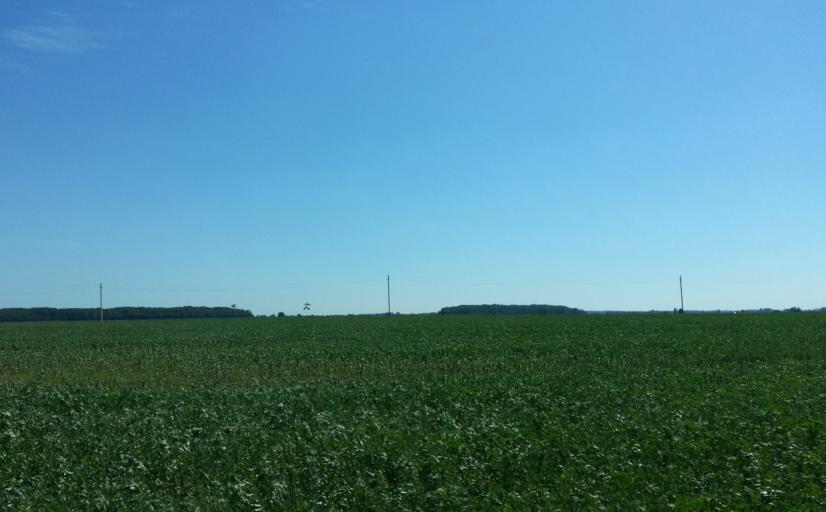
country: LT
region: Panevezys
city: Pasvalys
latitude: 56.2276
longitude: 24.4451
